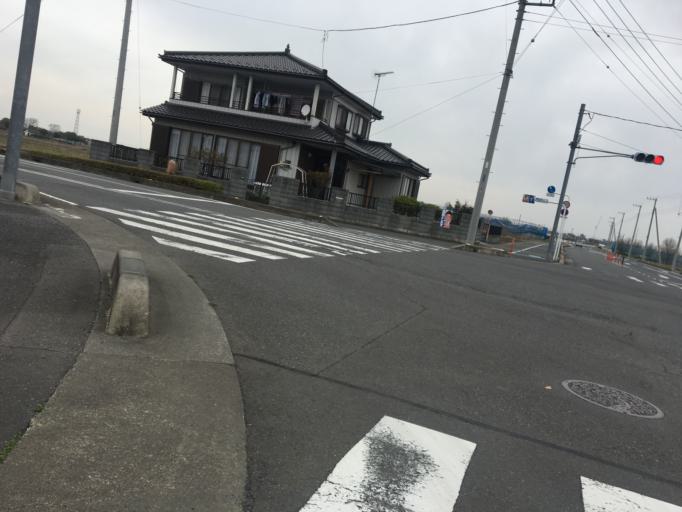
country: JP
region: Saitama
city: Kisai
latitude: 36.1050
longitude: 139.5814
